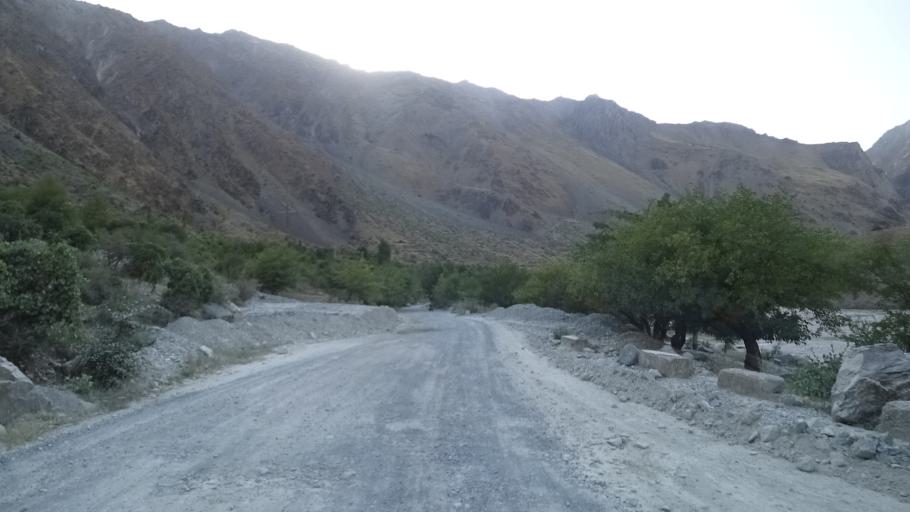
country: TJ
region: Gorno-Badakhshan
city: Qalaikhumb
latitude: 38.3866
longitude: 70.6776
